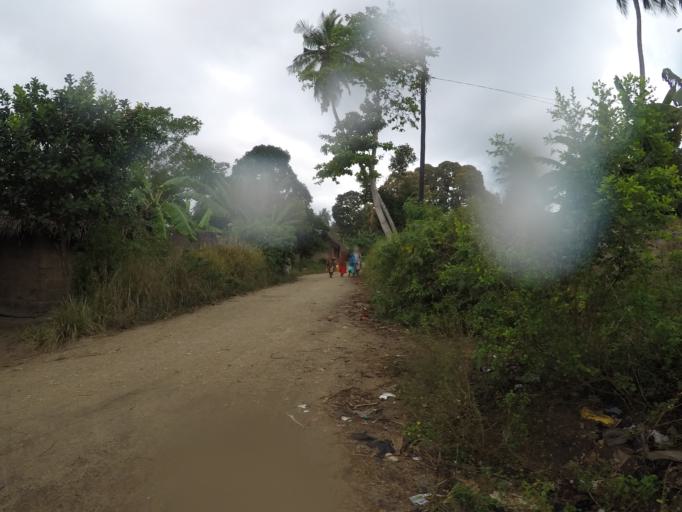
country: TZ
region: Zanzibar North
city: Mkokotoni
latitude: -5.9519
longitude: 39.1954
